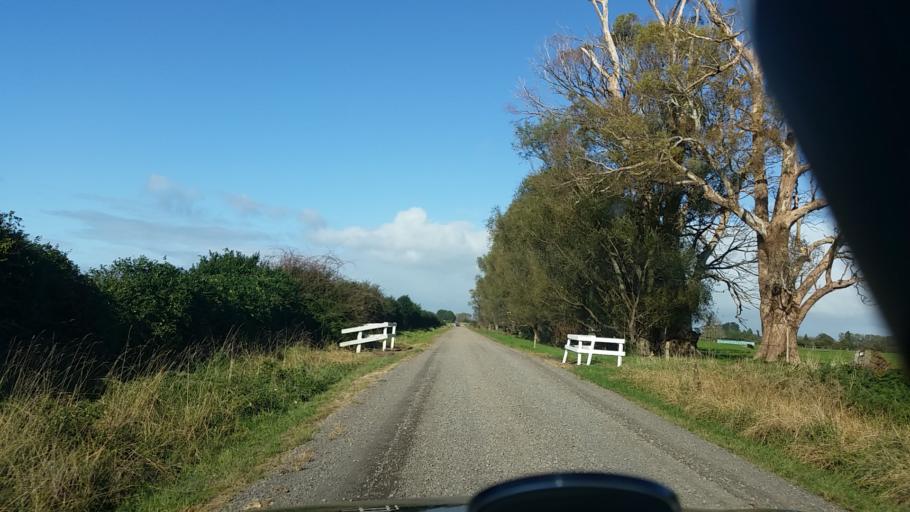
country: NZ
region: Bay of Plenty
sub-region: Western Bay of Plenty District
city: Katikati
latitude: -37.5879
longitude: 175.7132
